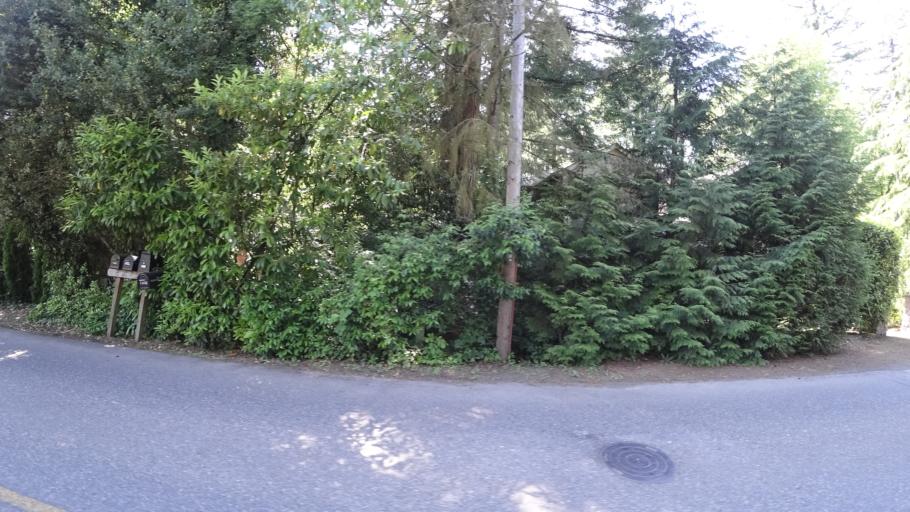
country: US
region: Oregon
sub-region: Clackamas County
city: Lake Oswego
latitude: 45.4247
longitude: -122.6958
